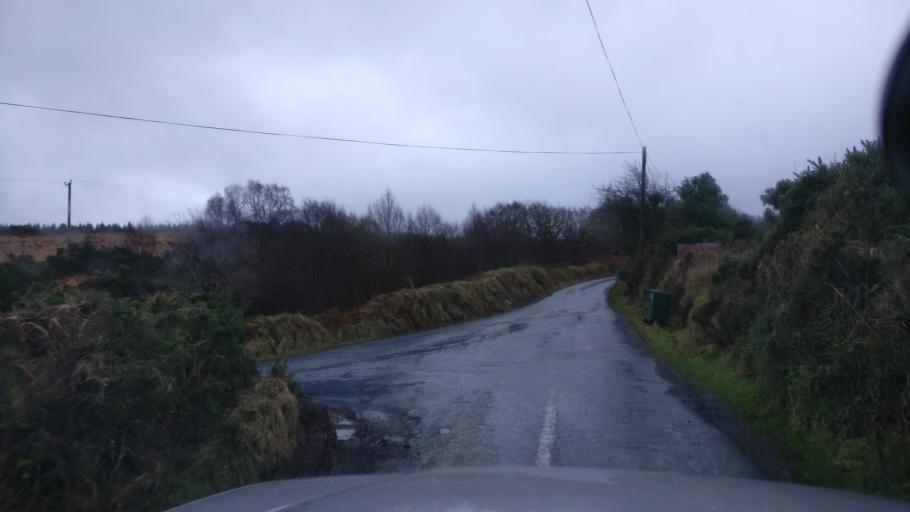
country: IE
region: Connaught
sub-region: County Galway
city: Loughrea
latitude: 53.1485
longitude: -8.6144
